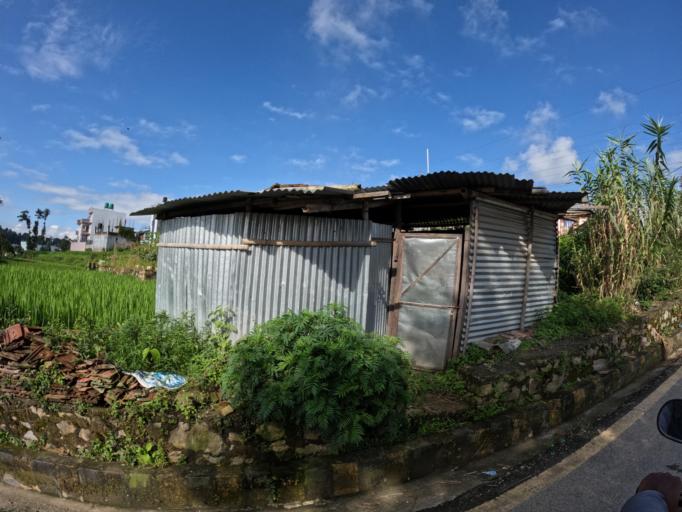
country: NP
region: Central Region
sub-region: Bagmati Zone
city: Kathmandu
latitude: 27.7597
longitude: 85.3337
